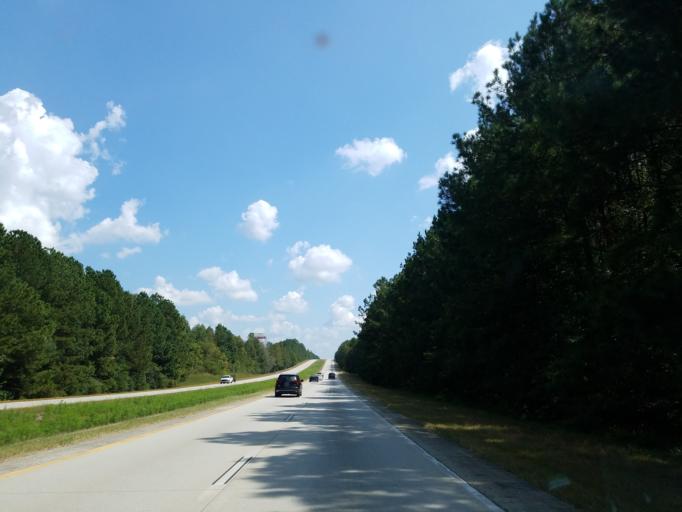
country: US
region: Georgia
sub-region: Barrow County
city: Auburn
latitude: 33.9587
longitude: -83.7863
